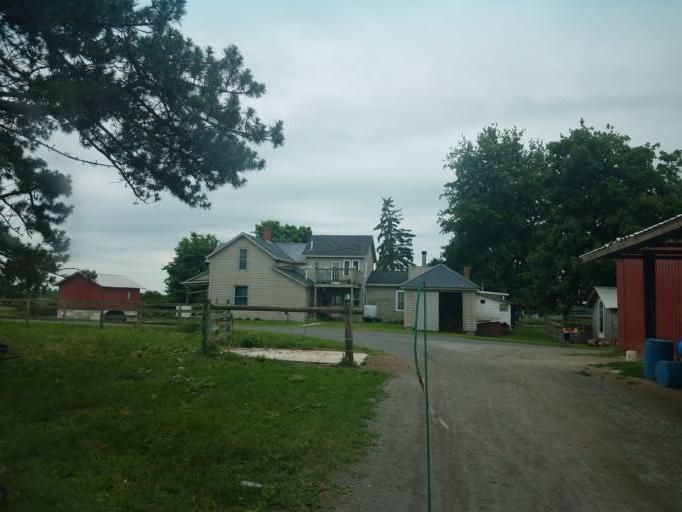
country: US
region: Ohio
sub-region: Hardin County
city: Kenton
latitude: 40.6332
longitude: -83.5385
